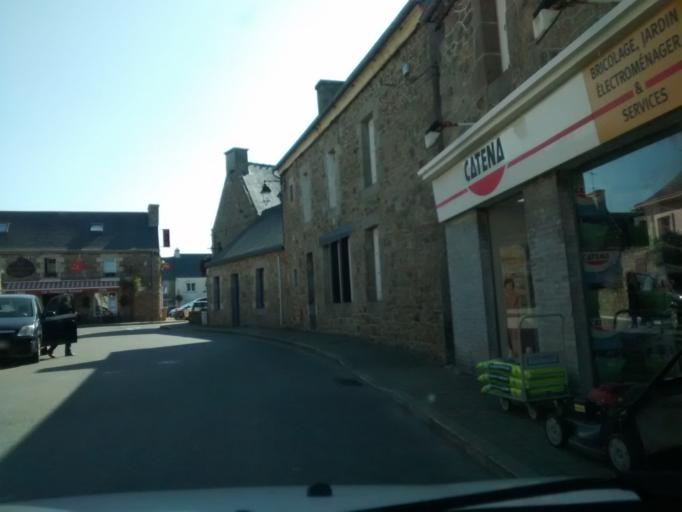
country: FR
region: Brittany
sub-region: Departement des Cotes-d'Armor
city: Pleubian
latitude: 48.8421
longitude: -3.1400
